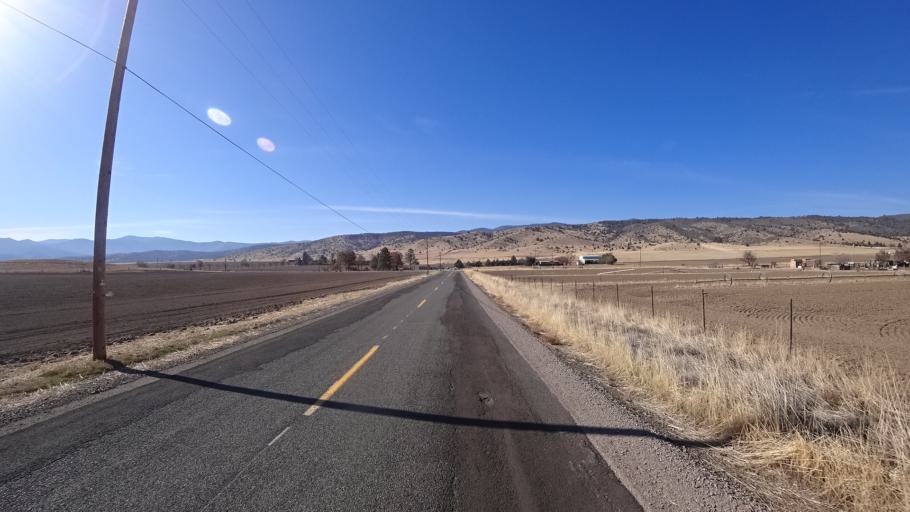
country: US
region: California
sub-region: Siskiyou County
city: Montague
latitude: 41.5747
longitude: -122.5454
